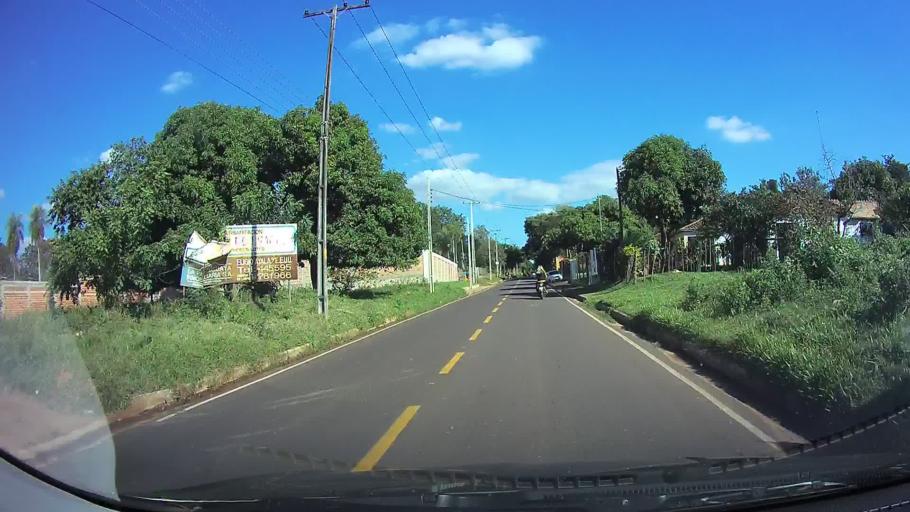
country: PY
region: Central
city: Limpio
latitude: -25.1994
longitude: -57.4782
